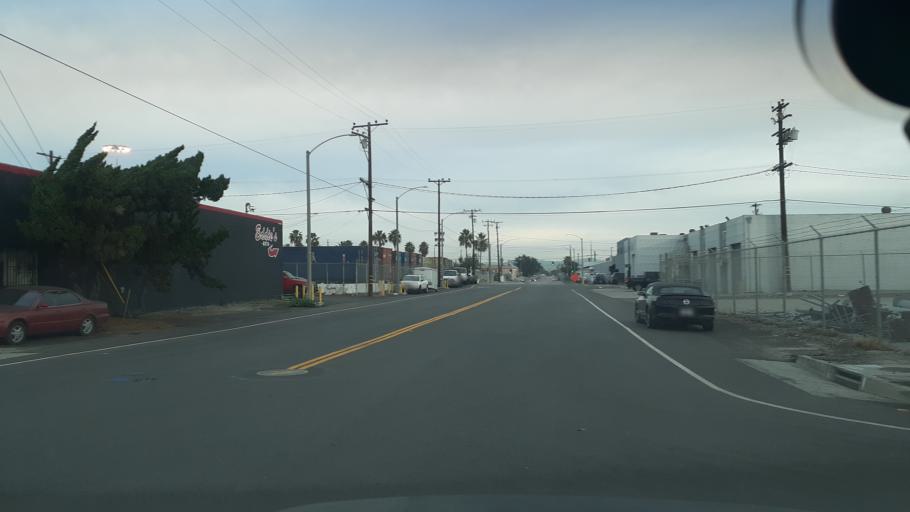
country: US
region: California
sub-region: Los Angeles County
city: Long Beach
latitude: 33.7807
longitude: -118.2105
